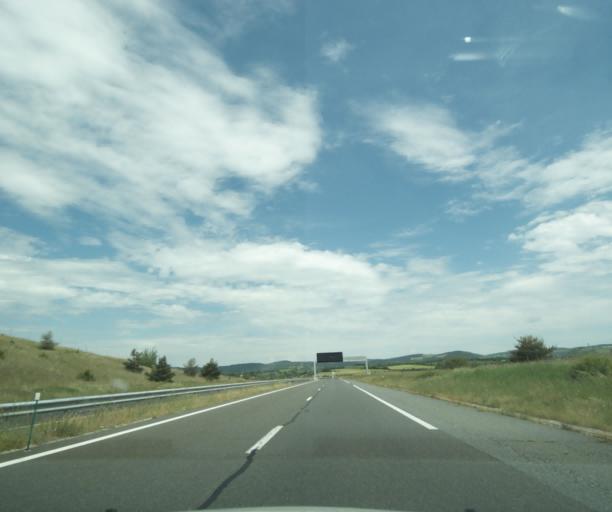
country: FR
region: Midi-Pyrenees
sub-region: Departement de l'Aveyron
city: Severac-le-Chateau
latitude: 44.2997
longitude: 3.1007
